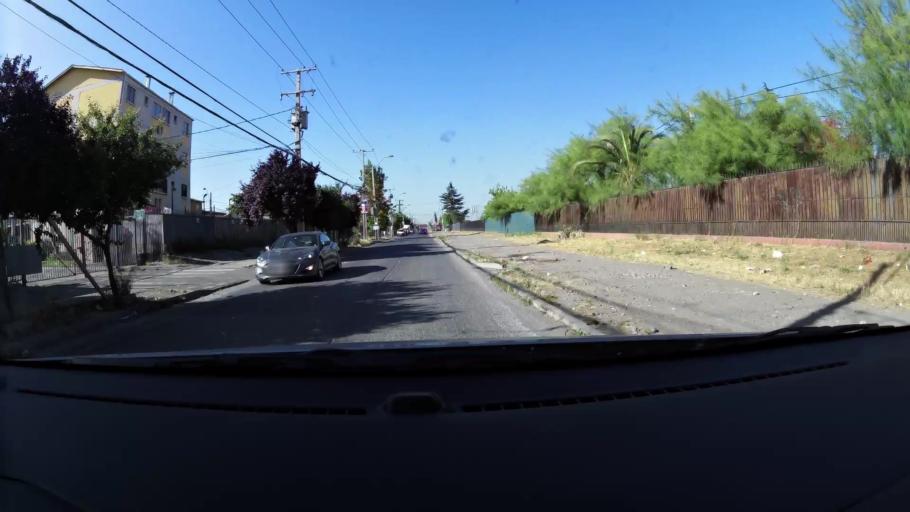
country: CL
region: Santiago Metropolitan
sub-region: Provincia de Maipo
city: San Bernardo
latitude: -33.5477
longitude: -70.6893
